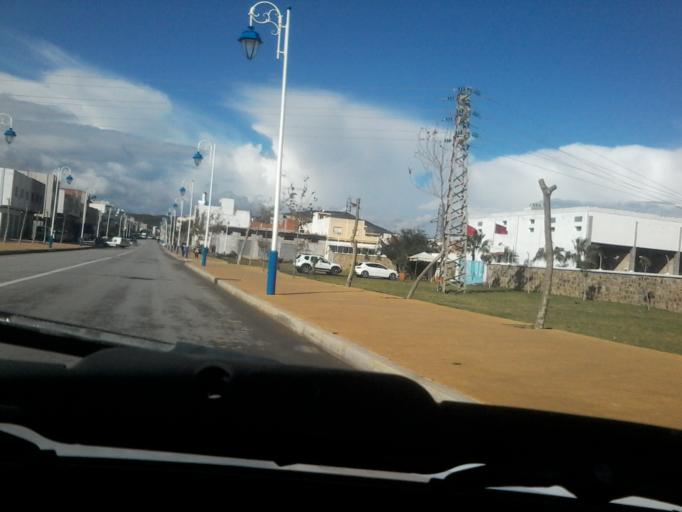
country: MA
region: Tanger-Tetouan
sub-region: Tetouan
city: Martil
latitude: 35.6959
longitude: -5.3449
